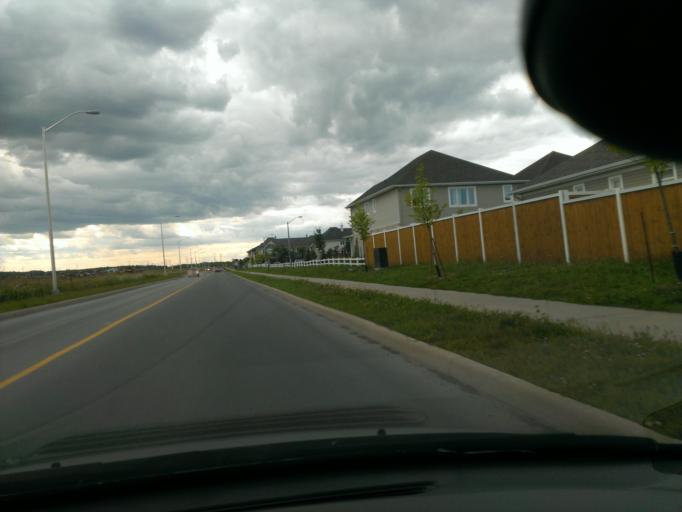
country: CA
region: Ontario
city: Ottawa
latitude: 45.4480
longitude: -75.4907
